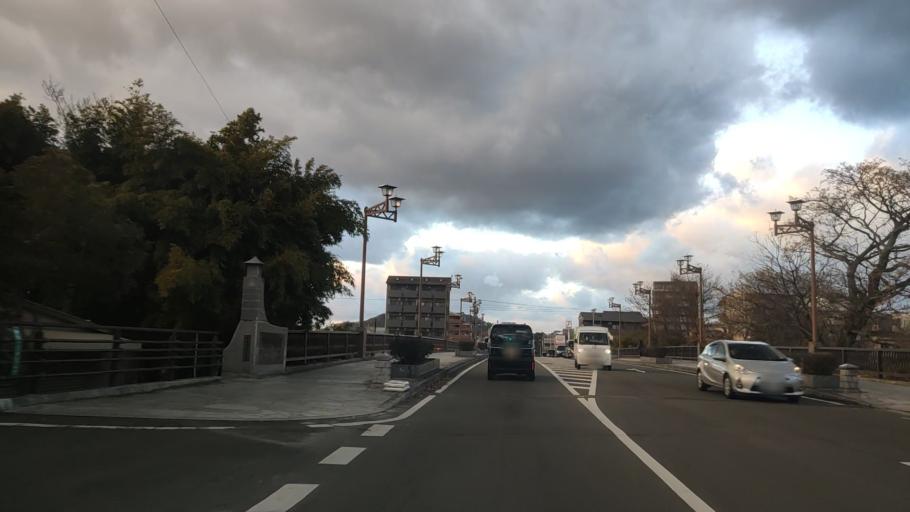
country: JP
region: Ehime
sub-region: Shikoku-chuo Shi
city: Matsuyama
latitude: 33.8391
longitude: 132.7861
